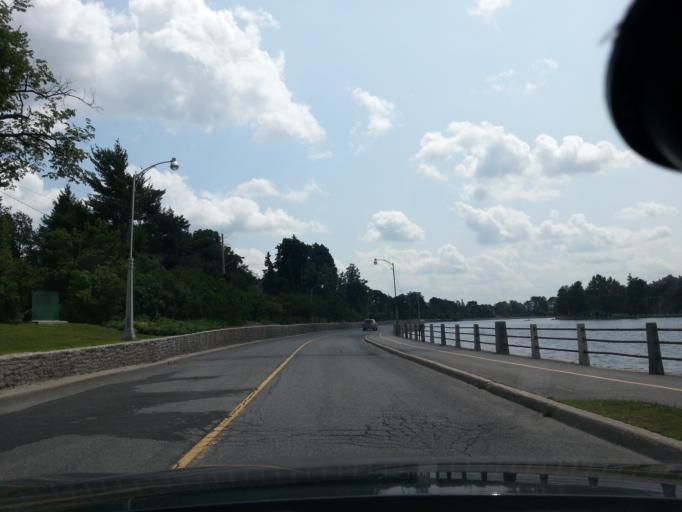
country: CA
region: Ontario
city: Ottawa
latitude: 45.4036
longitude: -75.6797
